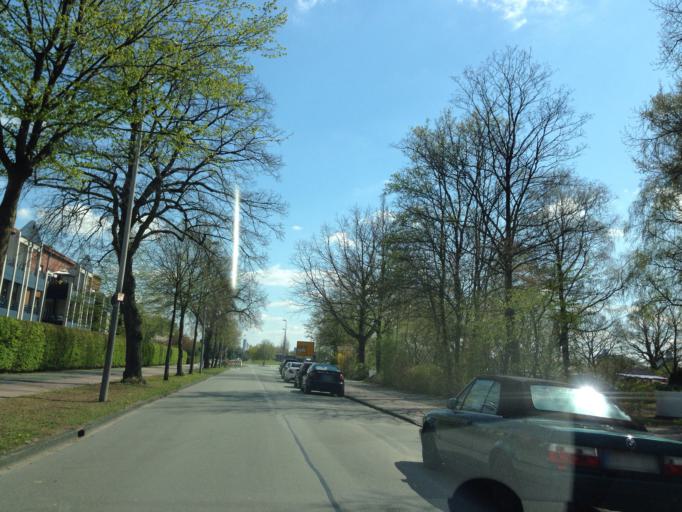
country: DE
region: North Rhine-Westphalia
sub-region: Regierungsbezirk Munster
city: Muenster
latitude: 51.9748
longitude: 7.5881
